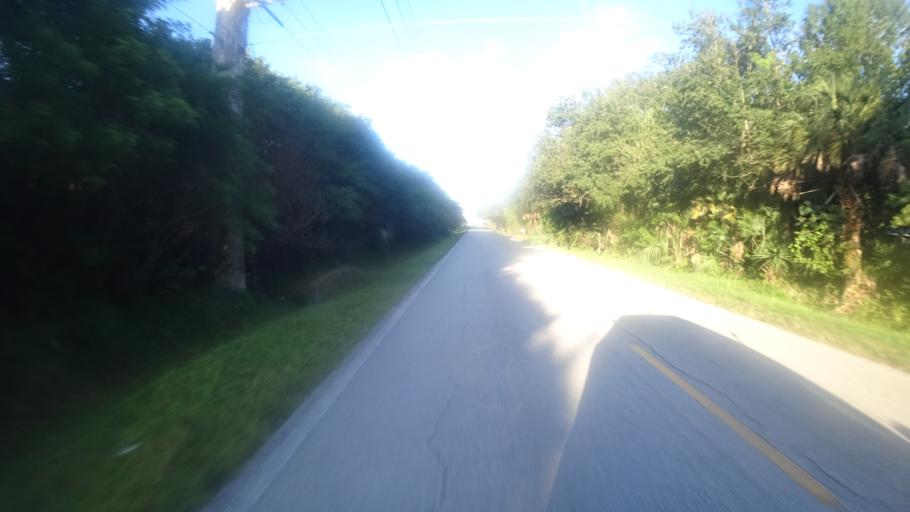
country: US
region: Florida
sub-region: Manatee County
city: Samoset
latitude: 27.4618
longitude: -82.5016
